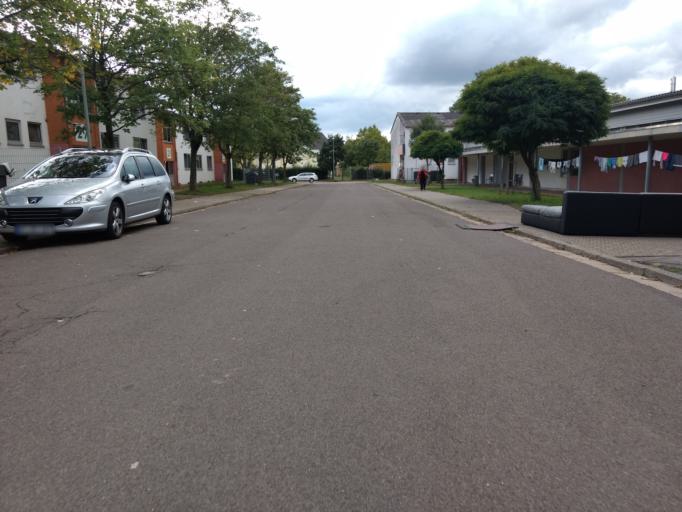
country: DE
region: Saarland
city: Lebach
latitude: 49.4055
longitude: 6.8986
